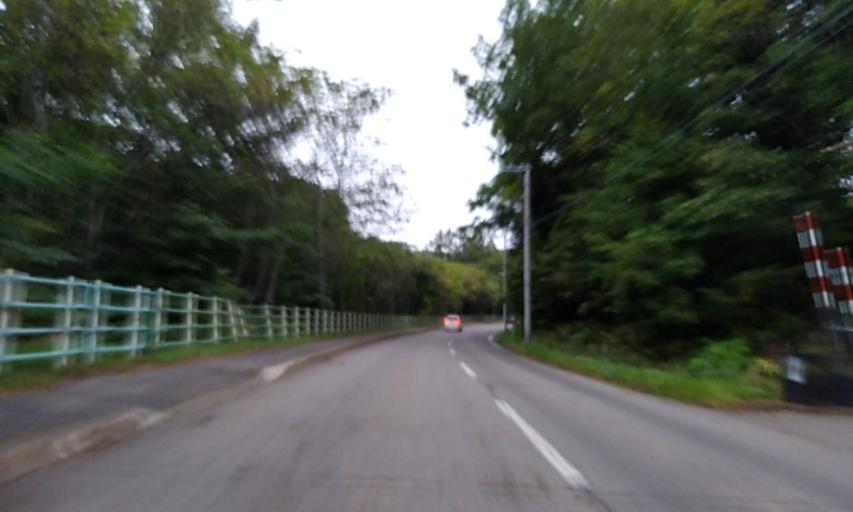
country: JP
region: Hokkaido
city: Abashiri
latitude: 43.9999
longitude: 144.2292
